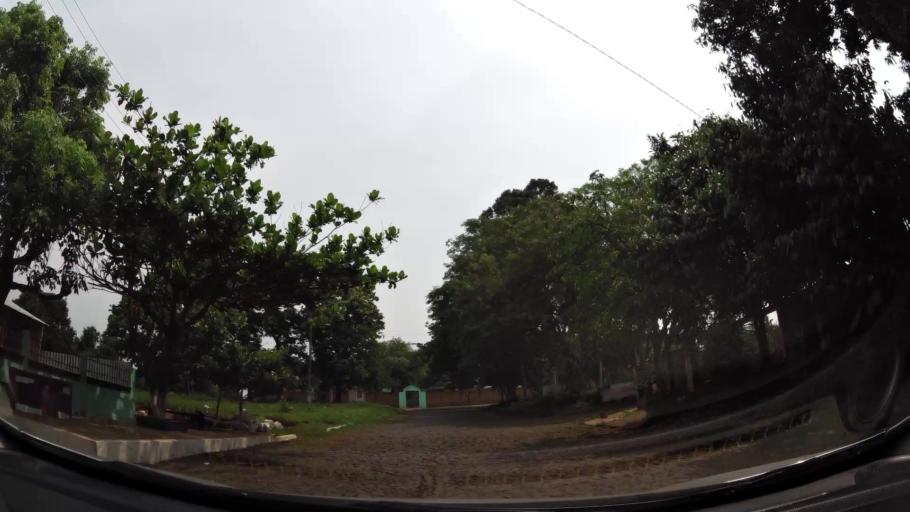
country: BR
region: Parana
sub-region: Foz Do Iguacu
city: Foz do Iguacu
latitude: -25.5670
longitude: -54.6074
